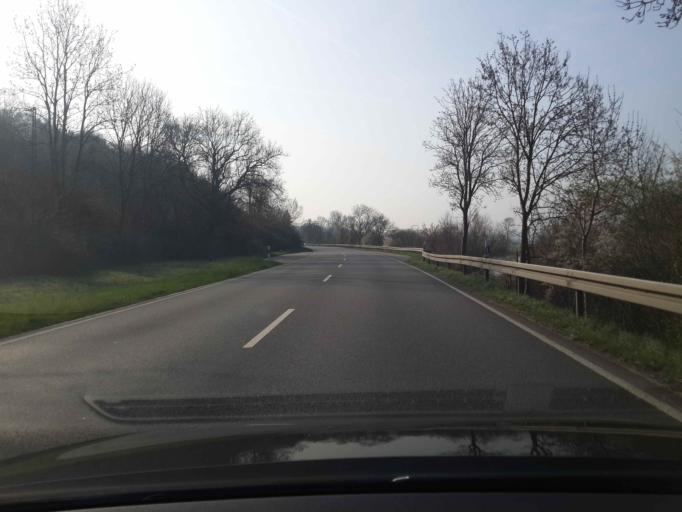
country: DE
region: Baden-Wuerttemberg
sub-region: Regierungsbezirk Stuttgart
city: Gundelsheim
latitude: 49.2652
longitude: 9.1543
